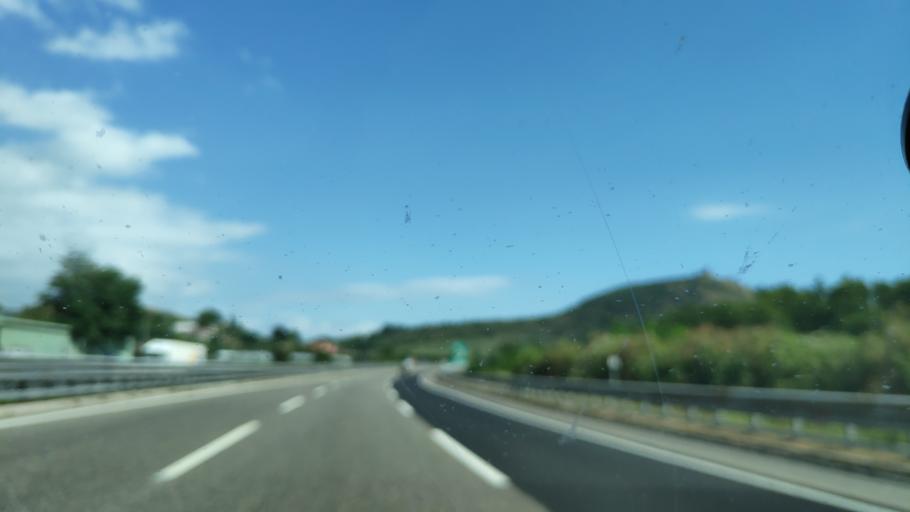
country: IT
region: Campania
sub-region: Provincia di Salerno
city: San Mango Piemonte
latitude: 40.6851
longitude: 14.8526
